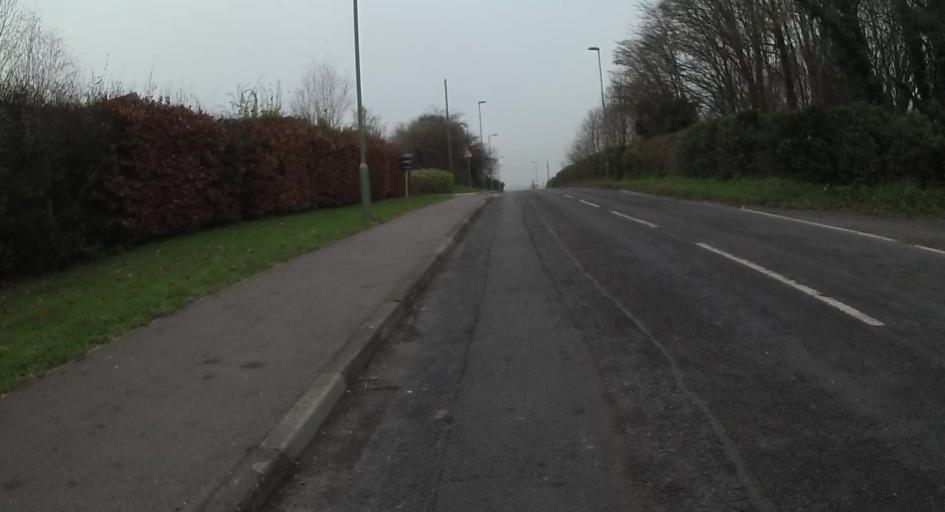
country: GB
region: England
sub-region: Hampshire
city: Kings Worthy
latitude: 51.0985
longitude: -1.2954
